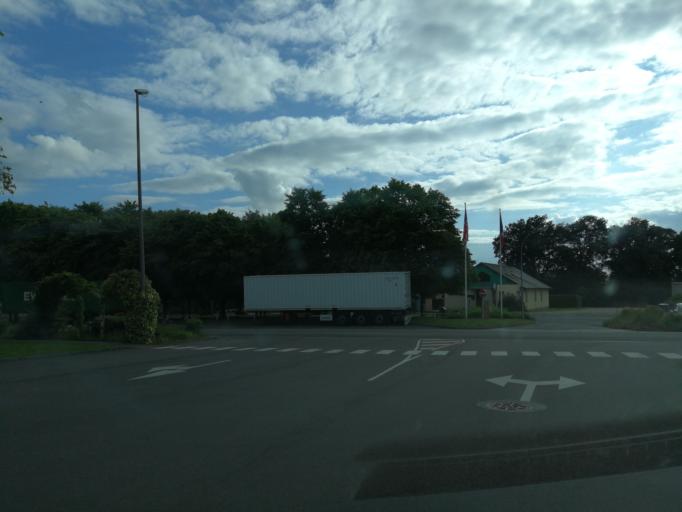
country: FR
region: Haute-Normandie
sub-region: Departement de l'Eure
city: Le Neubourg
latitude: 49.1424
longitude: 0.9034
